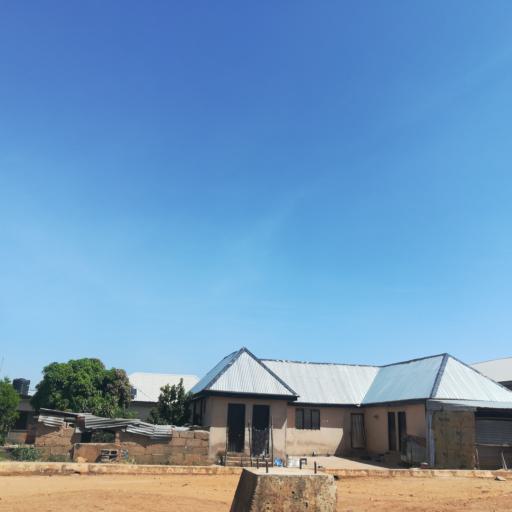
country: NG
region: Plateau
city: Bukuru
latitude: 9.7879
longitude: 8.8754
